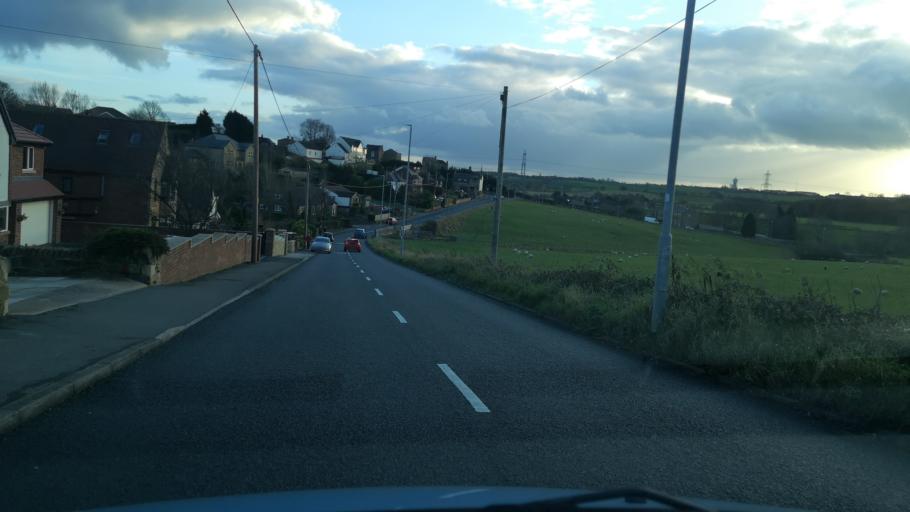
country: GB
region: England
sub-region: City and Borough of Leeds
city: Morley
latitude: 53.7188
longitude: -1.5816
